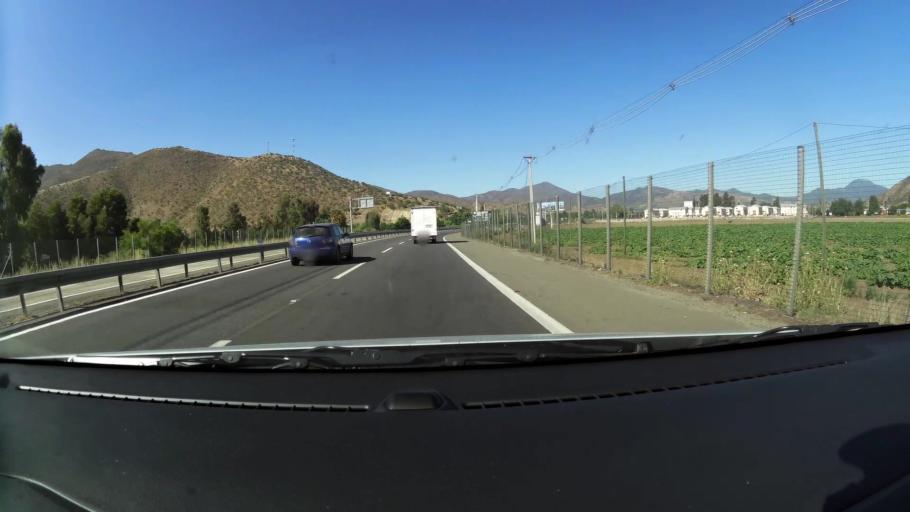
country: CL
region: Santiago Metropolitan
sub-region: Provincia de Chacabuco
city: Lampa
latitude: -33.4075
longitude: -71.1232
